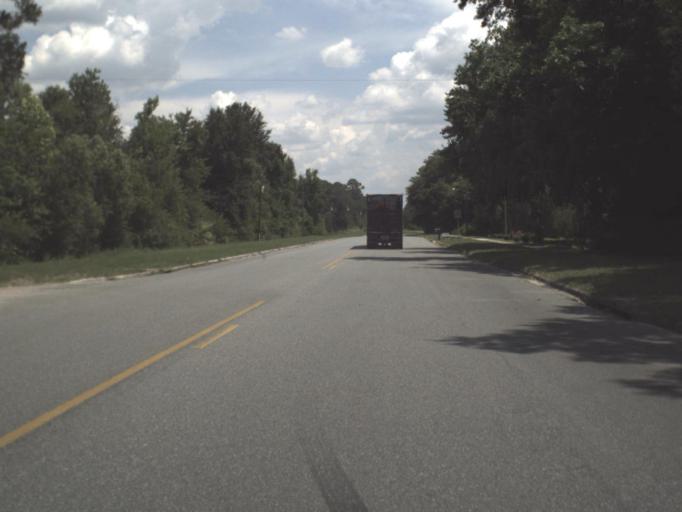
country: US
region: Florida
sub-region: Bradford County
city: Starke
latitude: 30.0413
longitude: -82.0638
